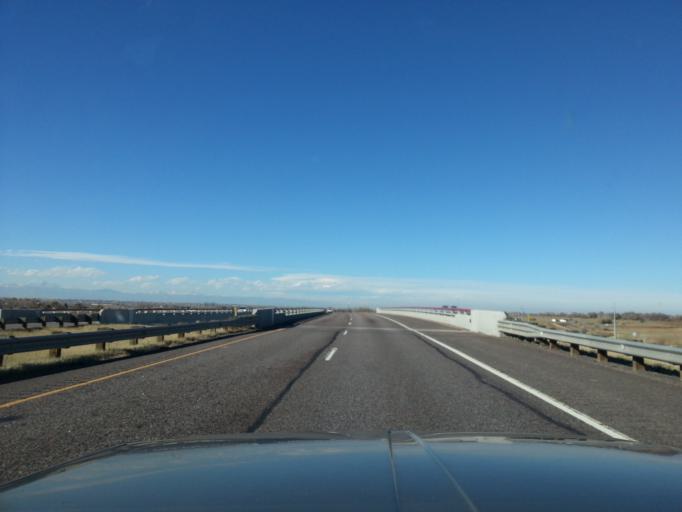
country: US
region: Colorado
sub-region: Adams County
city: Brighton
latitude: 39.9135
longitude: -104.7813
